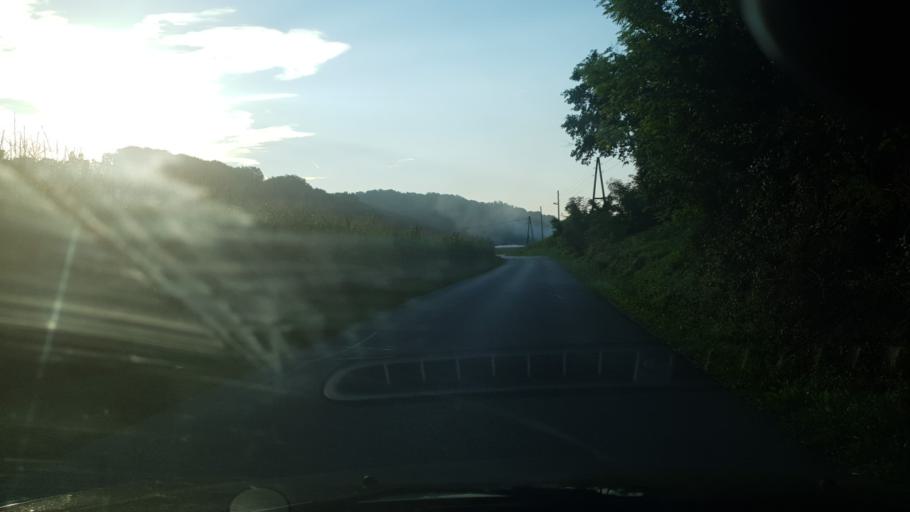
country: HR
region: Krapinsko-Zagorska
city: Zabok
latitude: 46.0866
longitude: 15.8874
